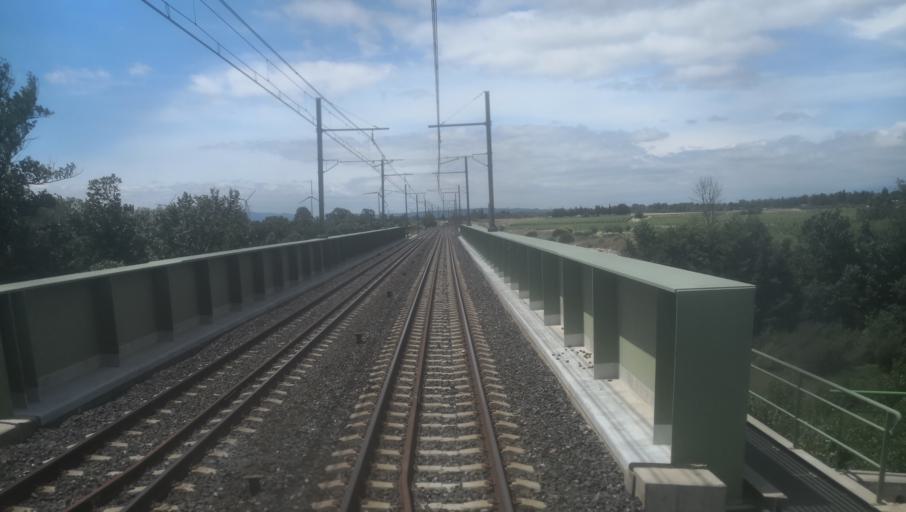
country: FR
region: Languedoc-Roussillon
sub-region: Departement de l'Aude
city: Canet
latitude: 43.2086
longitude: 2.8653
